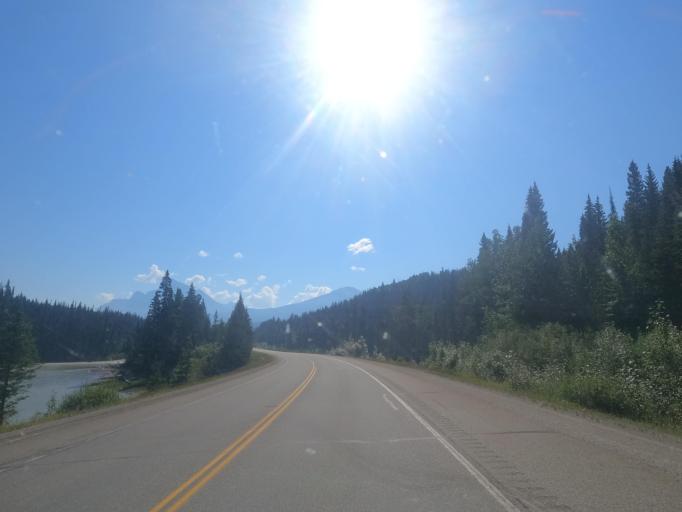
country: CA
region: Alberta
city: Jasper Park Lodge
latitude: 52.8598
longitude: -118.6388
